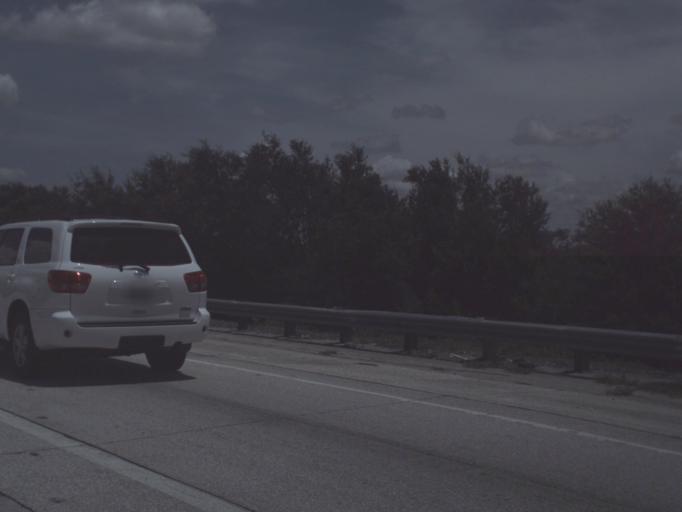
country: US
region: Florida
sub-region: Hillsborough County
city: Mango
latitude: 27.9946
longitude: -82.3262
